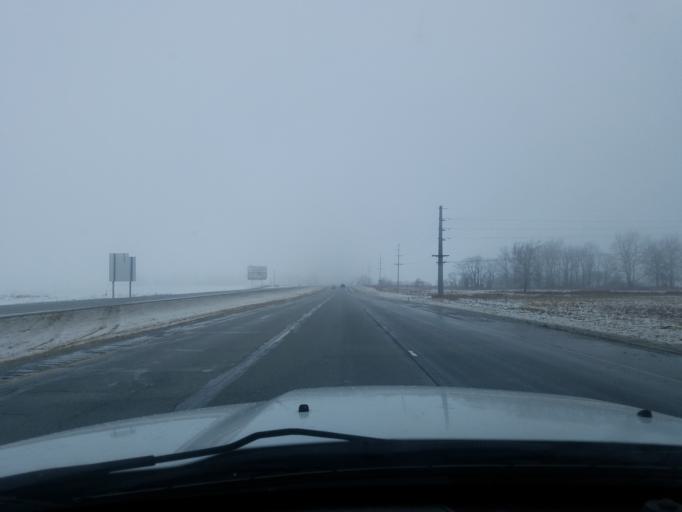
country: US
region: Indiana
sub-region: Tipton County
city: Tipton
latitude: 40.2793
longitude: -86.1267
